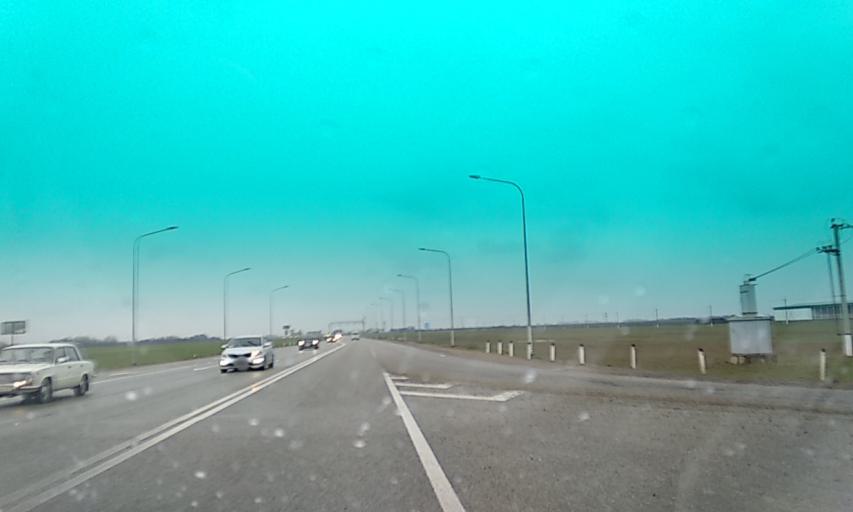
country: RU
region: Krasnodarskiy
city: Belorechensk
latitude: 44.8289
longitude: 39.8438
